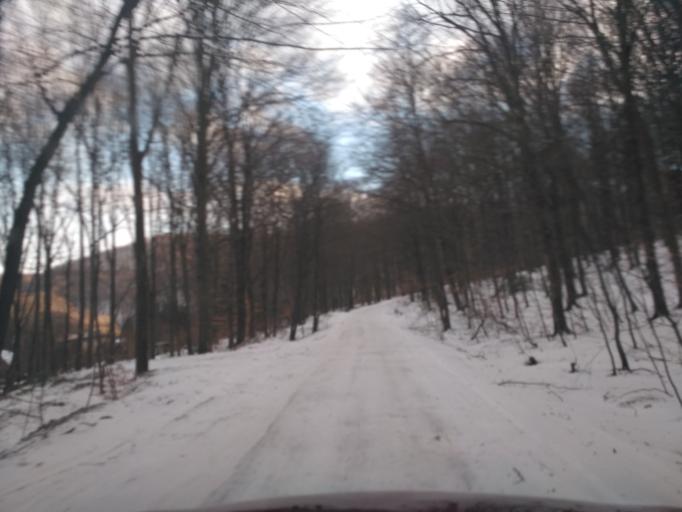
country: SK
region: Kosicky
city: Kosice
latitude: 48.7266
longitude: 21.1624
